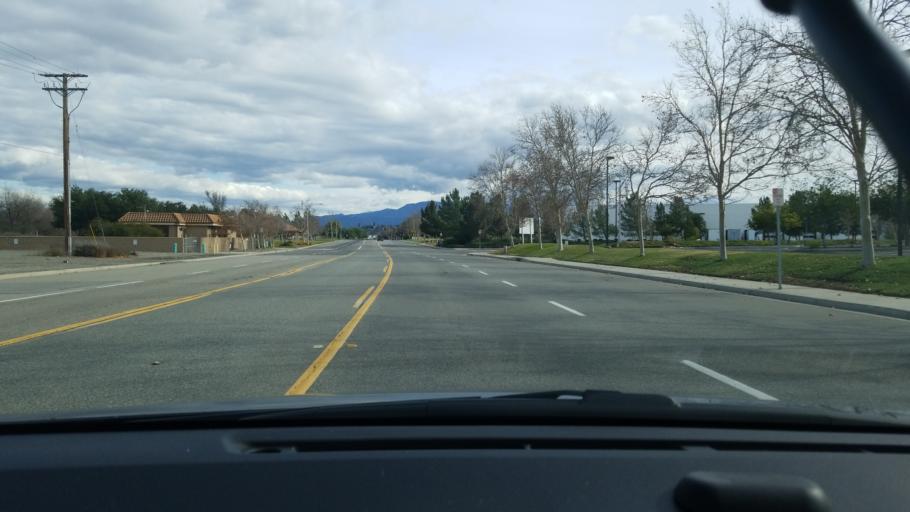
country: US
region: California
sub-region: Riverside County
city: Temecula
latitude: 33.5164
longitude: -117.1736
